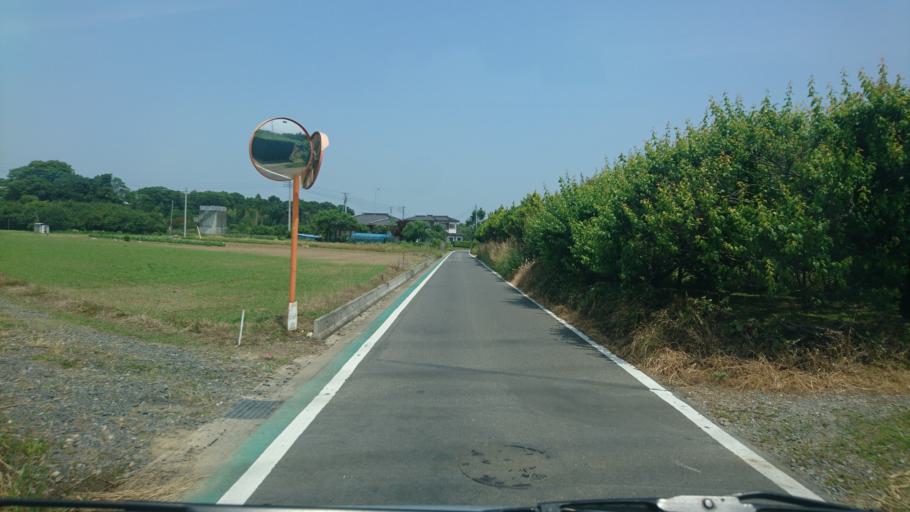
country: JP
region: Ibaraki
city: Mitsukaido
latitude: 36.0018
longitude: 139.9767
